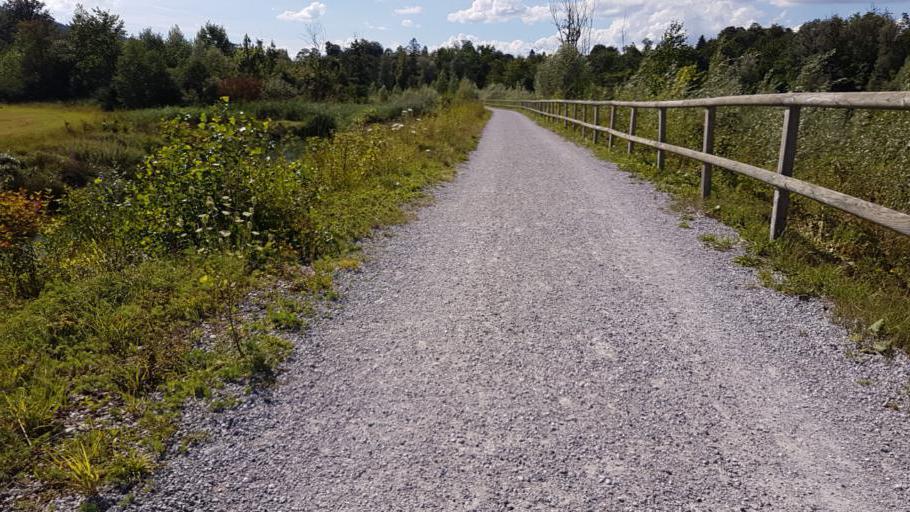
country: CH
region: Bern
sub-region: Bern-Mittelland District
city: Muri
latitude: 46.9240
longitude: 7.4868
